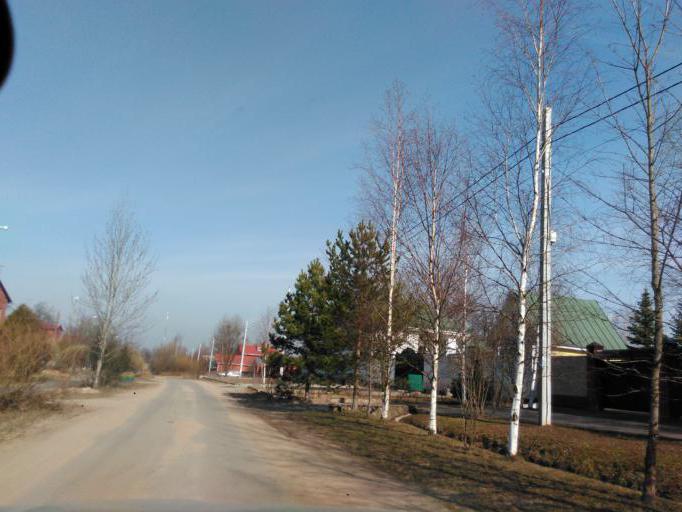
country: RU
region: Moskovskaya
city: Opalikha
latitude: 55.8753
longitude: 37.2710
